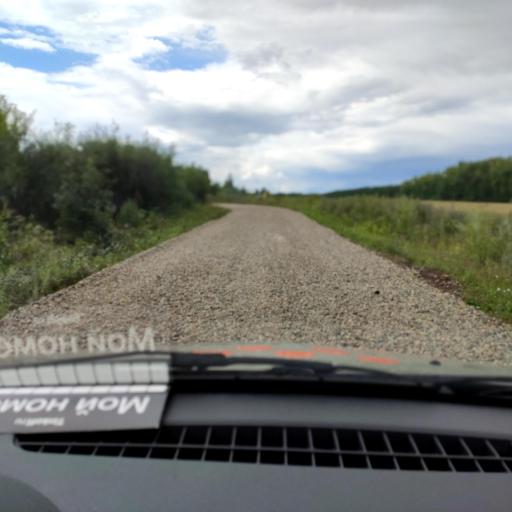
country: RU
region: Bashkortostan
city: Avdon
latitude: 54.5149
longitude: 55.8423
